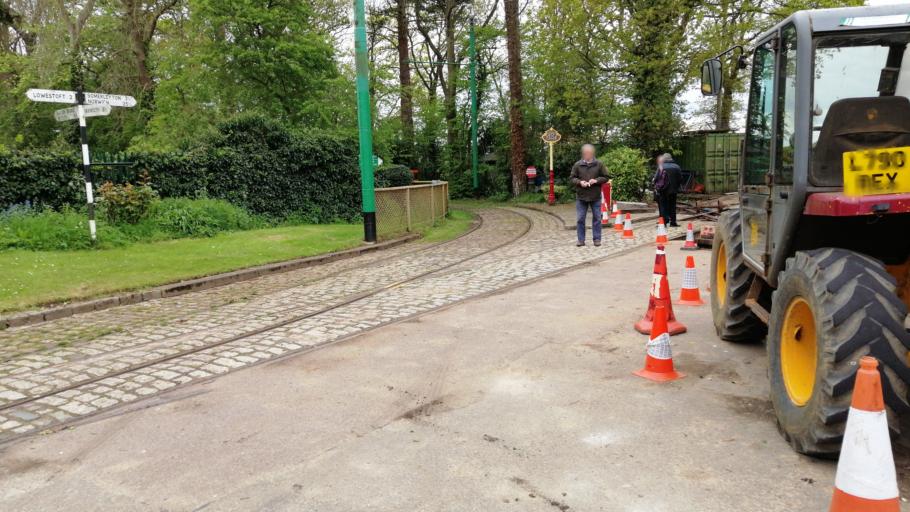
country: GB
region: England
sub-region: Suffolk
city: Kessingland
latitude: 52.4520
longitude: 1.6851
